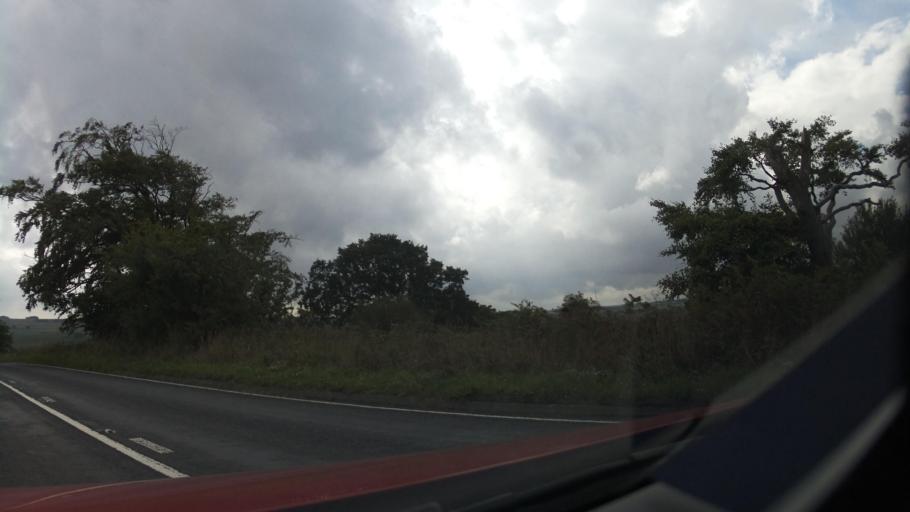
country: GB
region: England
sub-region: County Durham
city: Castleside
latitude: 54.8090
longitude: -1.8613
